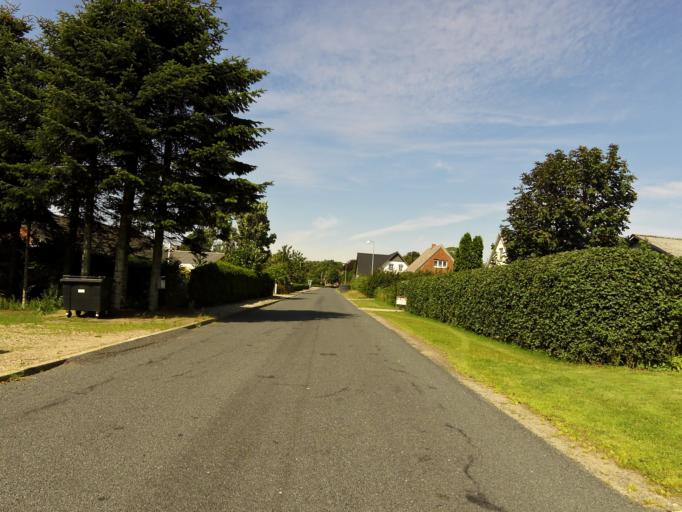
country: DK
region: South Denmark
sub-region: Haderslev Kommune
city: Gram
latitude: 55.2557
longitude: 8.9069
